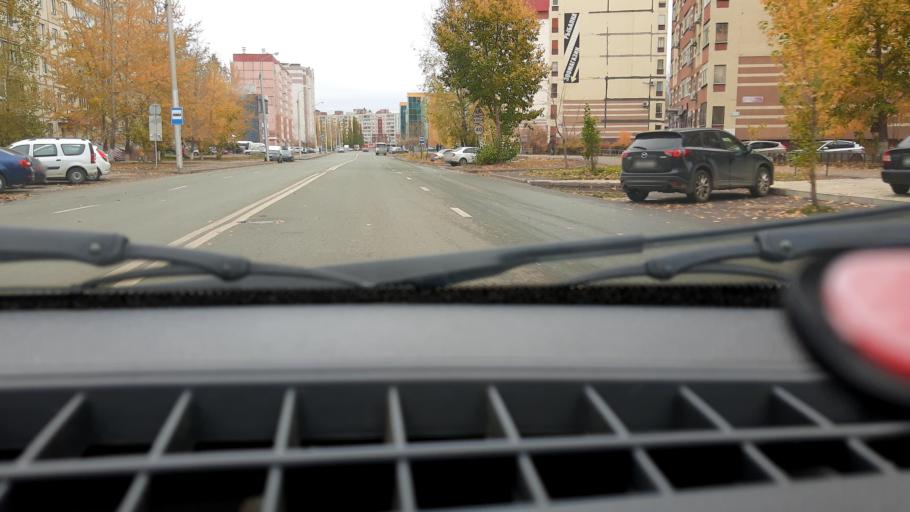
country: RU
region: Bashkortostan
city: Ufa
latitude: 54.7771
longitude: 56.0750
